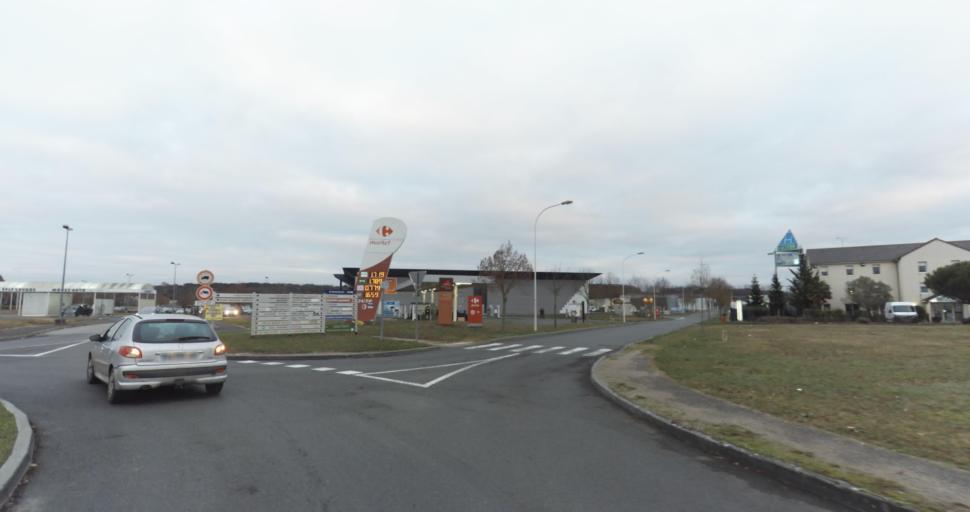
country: FR
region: Pays de la Loire
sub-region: Departement de Maine-et-Loire
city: Distre
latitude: 47.2315
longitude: -0.1195
